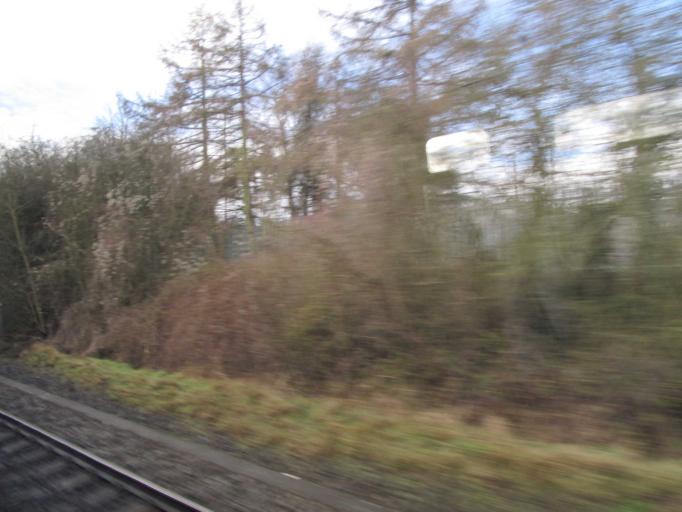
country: GB
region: England
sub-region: Hampshire
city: Basingstoke
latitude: 51.2784
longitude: -1.0687
